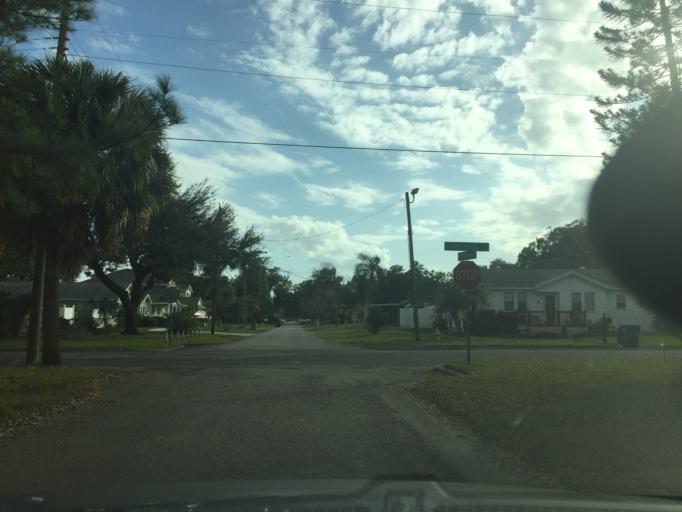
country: US
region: Florida
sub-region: Hillsborough County
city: Tampa
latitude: 27.9474
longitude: -82.4923
